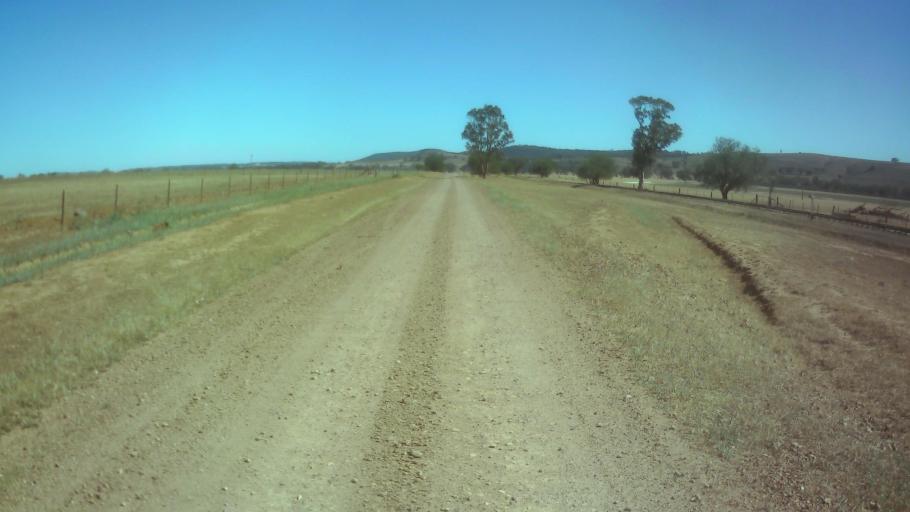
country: AU
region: New South Wales
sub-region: Weddin
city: Grenfell
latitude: -33.9581
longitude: 148.3031
